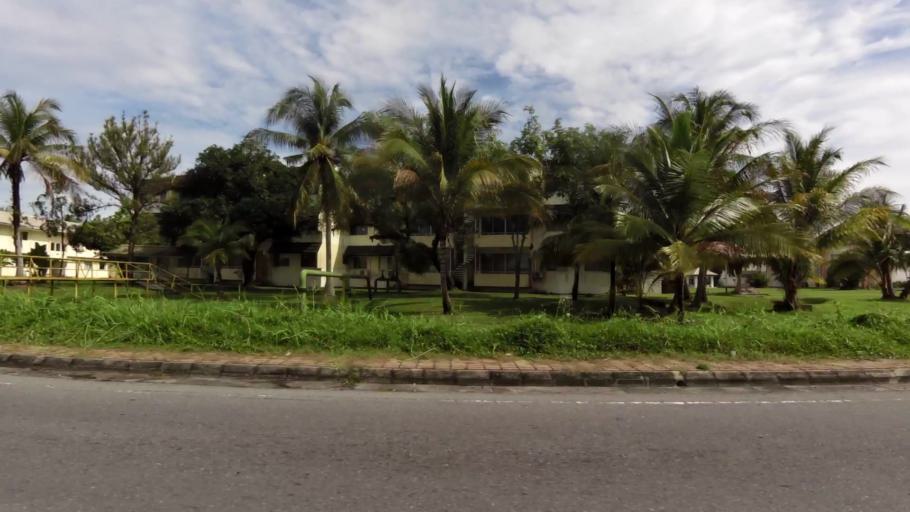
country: BN
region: Belait
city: Seria
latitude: 4.6139
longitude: 114.3245
